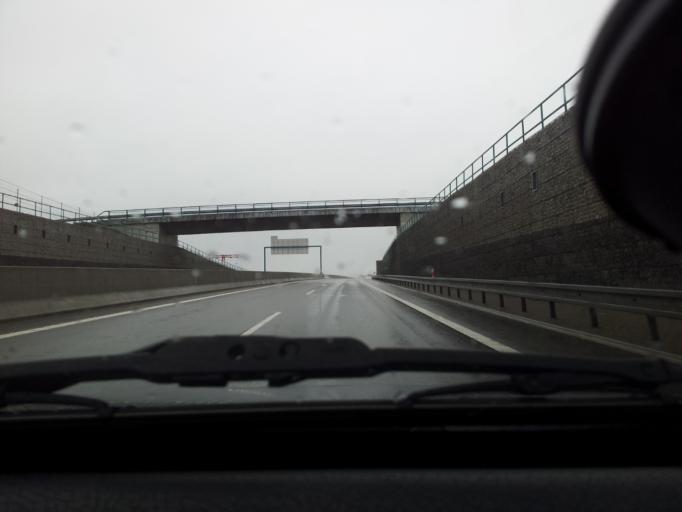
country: SK
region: Nitriansky
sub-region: Okres Nitra
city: Nitra
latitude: 48.2877
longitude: 18.0526
